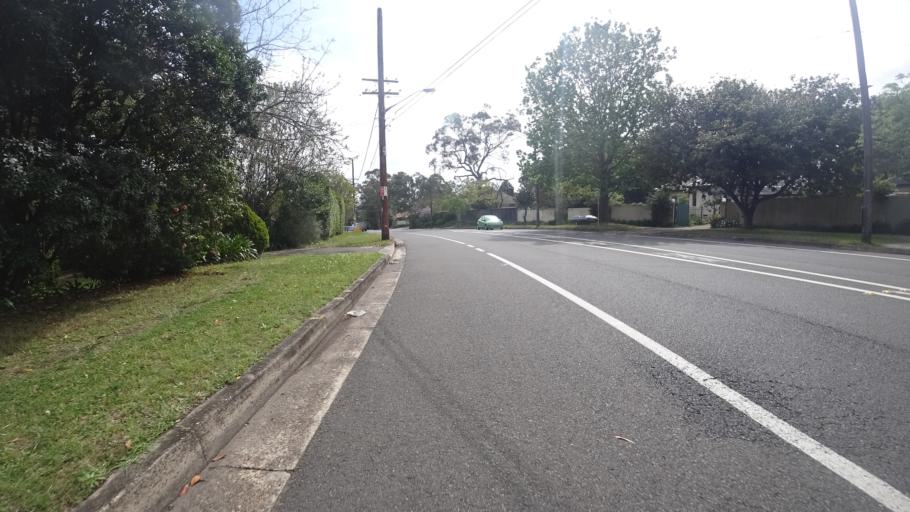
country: AU
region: New South Wales
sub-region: City of Sydney
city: North Turramurra
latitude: -33.7213
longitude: 151.1423
